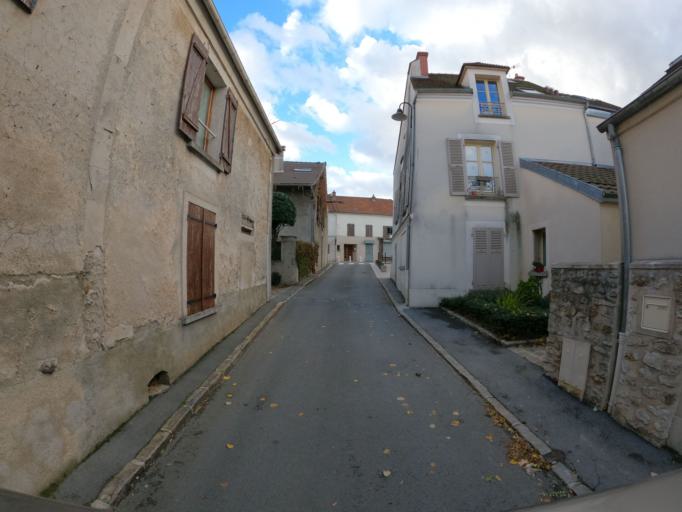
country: FR
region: Ile-de-France
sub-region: Departement de Seine-et-Marne
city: Chessy
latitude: 48.8797
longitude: 2.7645
